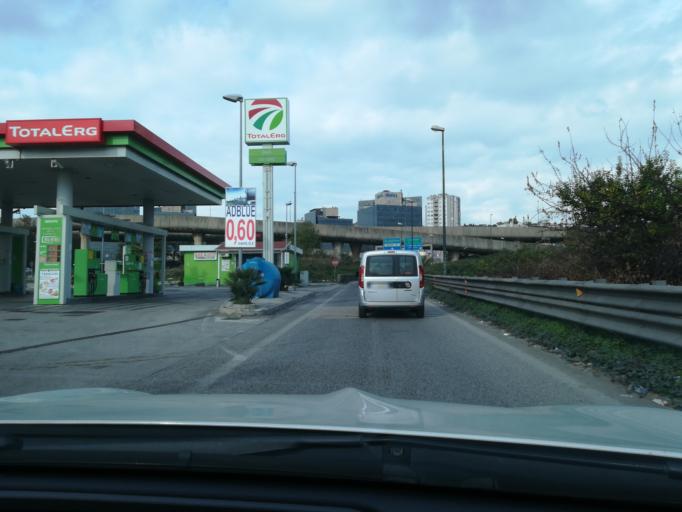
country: IT
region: Campania
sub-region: Provincia di Napoli
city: Casavatore
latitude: 40.8621
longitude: 14.2877
